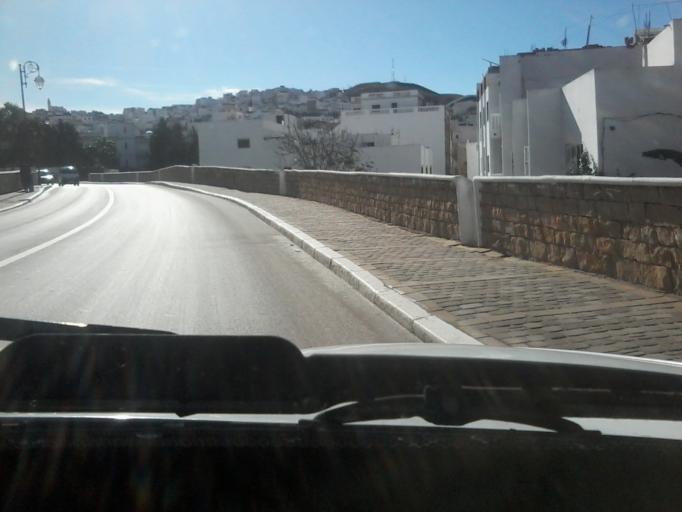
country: MA
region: Tanger-Tetouan
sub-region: Tetouan
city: Martil
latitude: 35.6874
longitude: -5.3308
